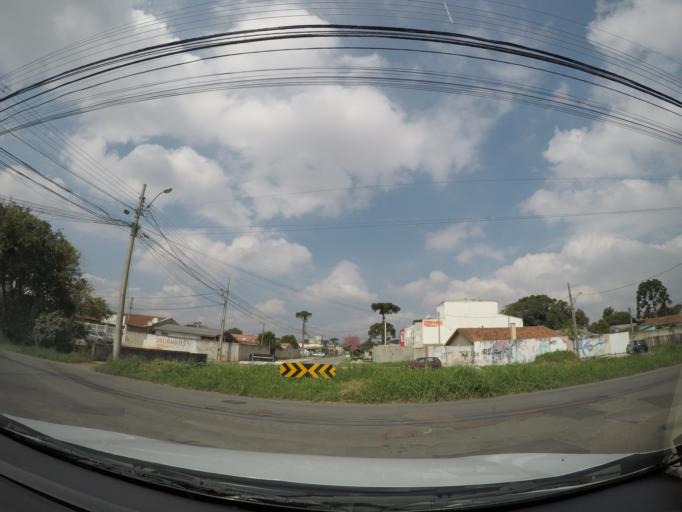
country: BR
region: Parana
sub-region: Sao Jose Dos Pinhais
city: Sao Jose dos Pinhais
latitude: -25.4902
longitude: -49.2542
